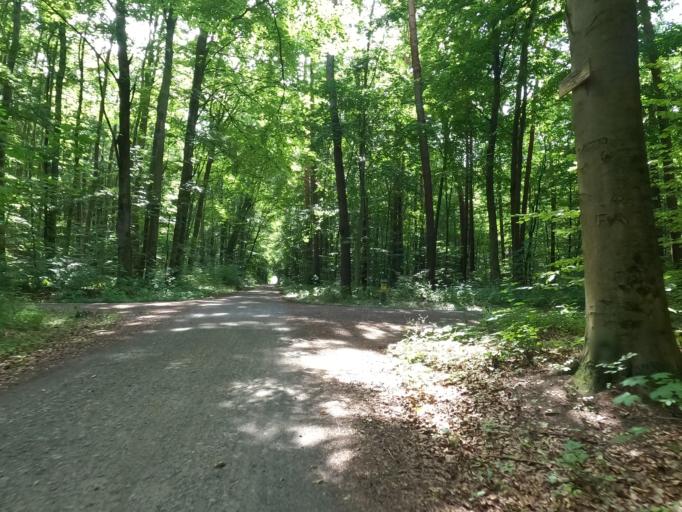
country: DE
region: Hesse
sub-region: Regierungsbezirk Darmstadt
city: Neu Isenburg
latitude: 50.0802
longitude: 8.7222
